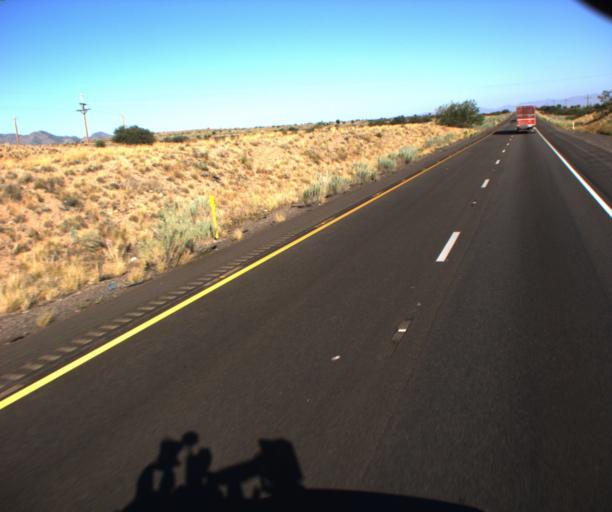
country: US
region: Arizona
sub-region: Mohave County
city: New Kingman-Butler
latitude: 35.1884
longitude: -113.8159
